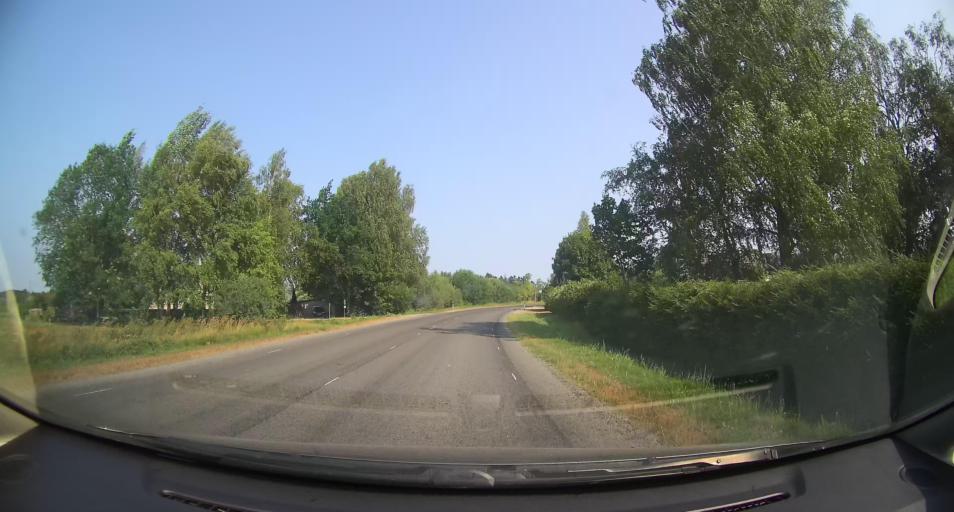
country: EE
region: Paernumaa
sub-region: Audru vald
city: Audru
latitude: 58.4627
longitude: 24.3135
